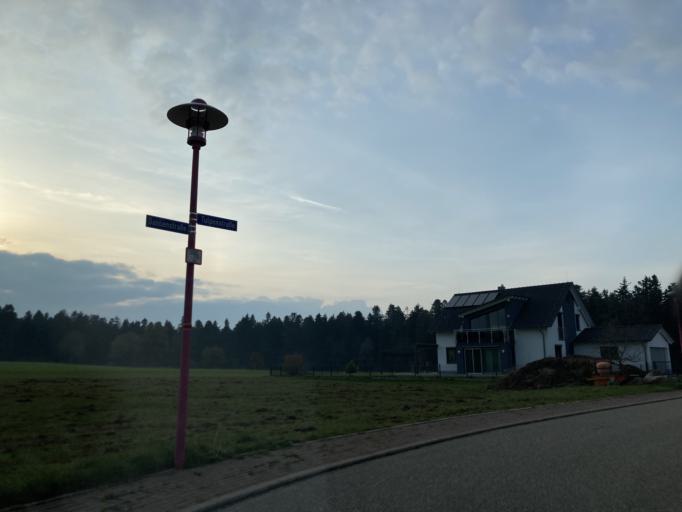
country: DE
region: Baden-Wuerttemberg
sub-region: Karlsruhe Region
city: Schomberg
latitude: 48.7905
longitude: 8.6381
